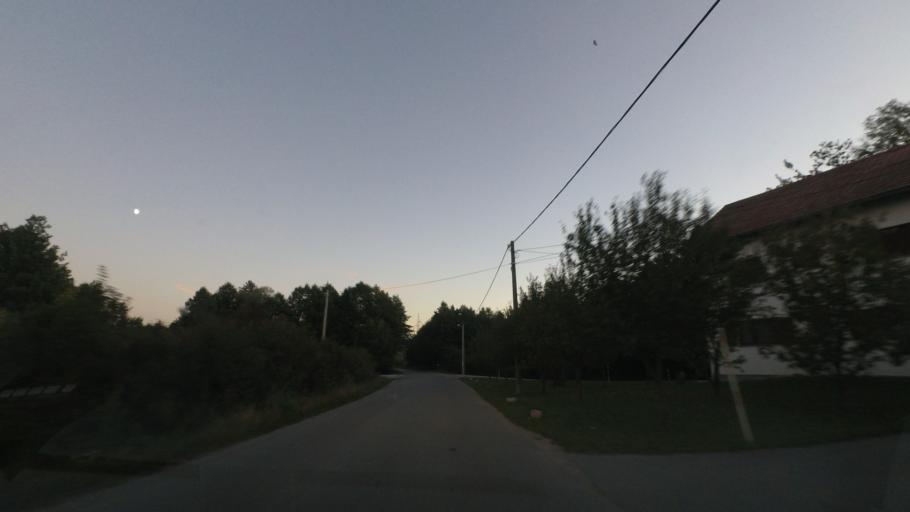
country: HR
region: Zadarska
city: Obrovac
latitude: 44.3729
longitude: 15.6463
